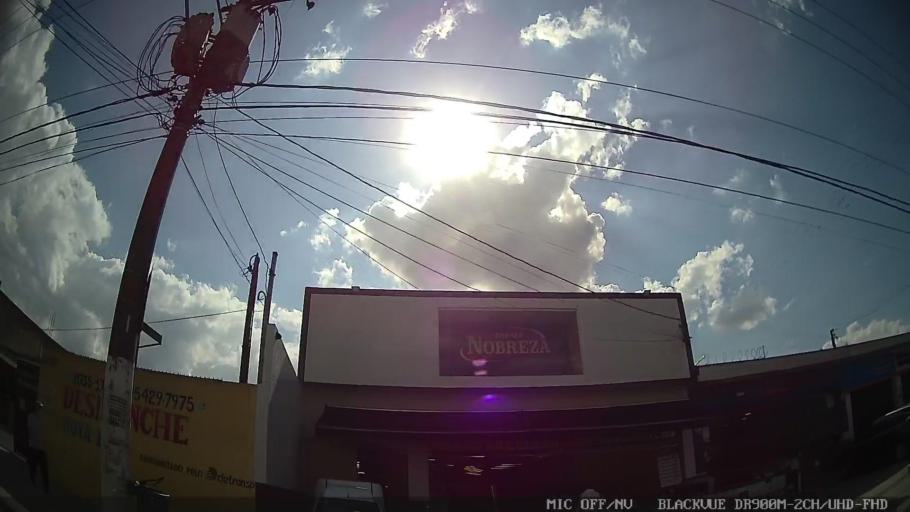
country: BR
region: Sao Paulo
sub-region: Ferraz De Vasconcelos
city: Ferraz de Vasconcelos
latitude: -23.5238
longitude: -46.4183
